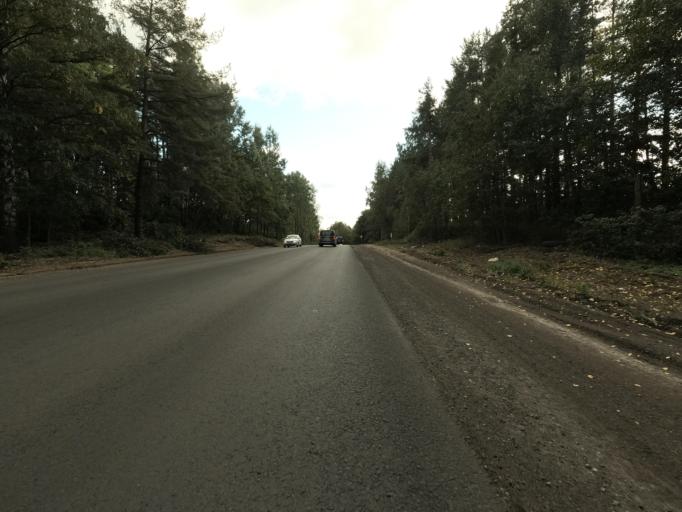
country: RU
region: Leningrad
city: Koltushi
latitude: 59.9508
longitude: 30.6569
